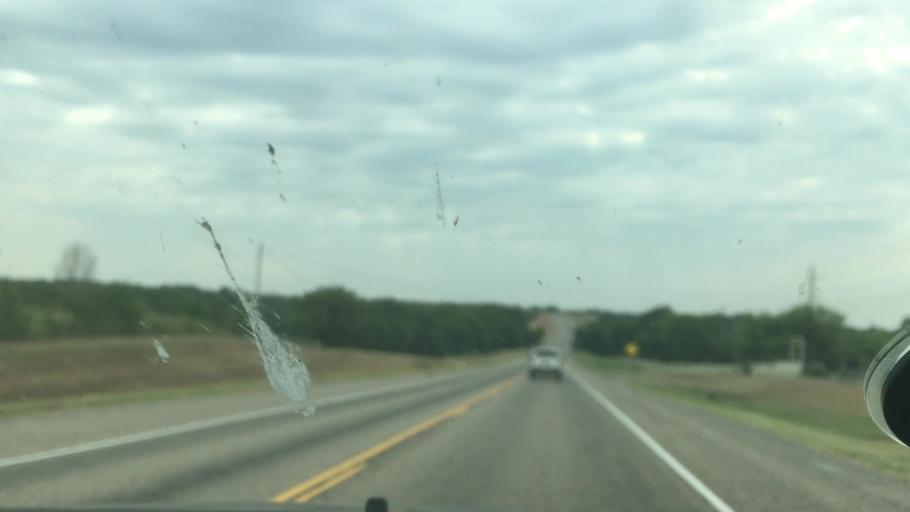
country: US
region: Texas
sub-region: Grayson County
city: Pottsboro
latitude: 33.8022
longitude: -96.6696
